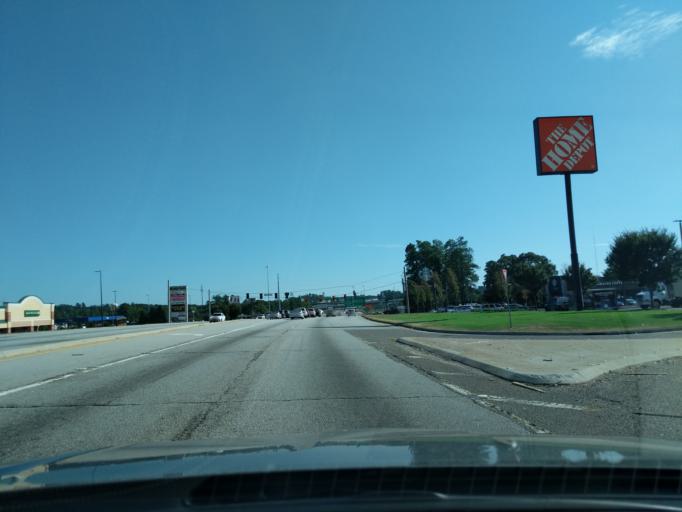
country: US
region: Georgia
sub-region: Columbia County
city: Martinez
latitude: 33.5024
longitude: -82.0881
